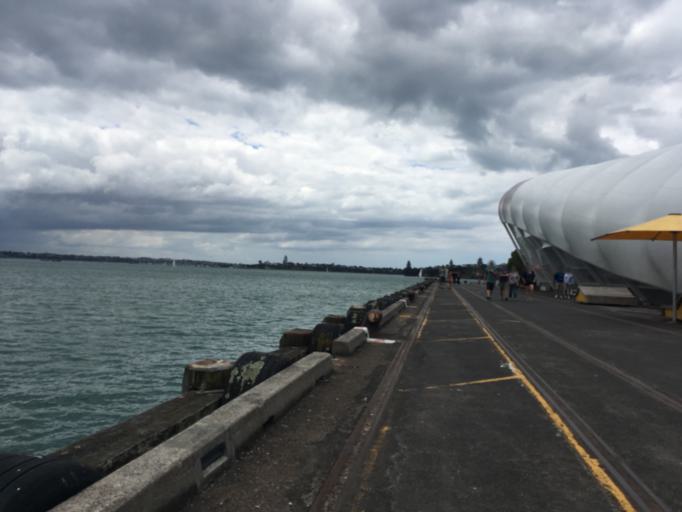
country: NZ
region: Auckland
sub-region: Auckland
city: Auckland
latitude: -36.8407
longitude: 174.7680
